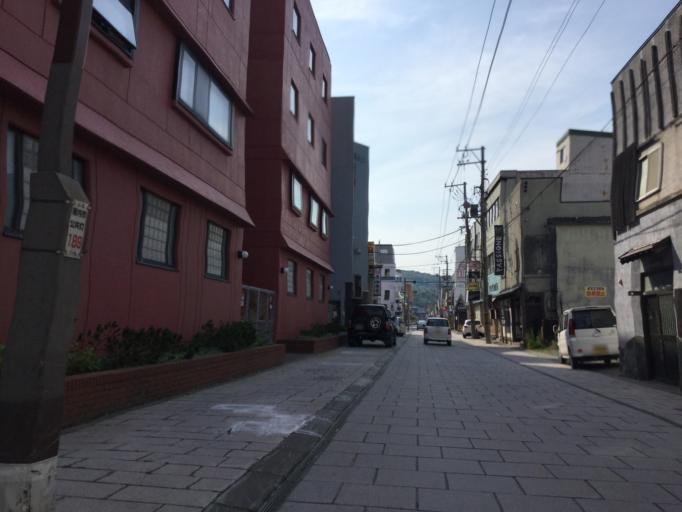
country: JP
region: Hokkaido
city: Wakkanai
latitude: 45.3976
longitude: 141.6862
